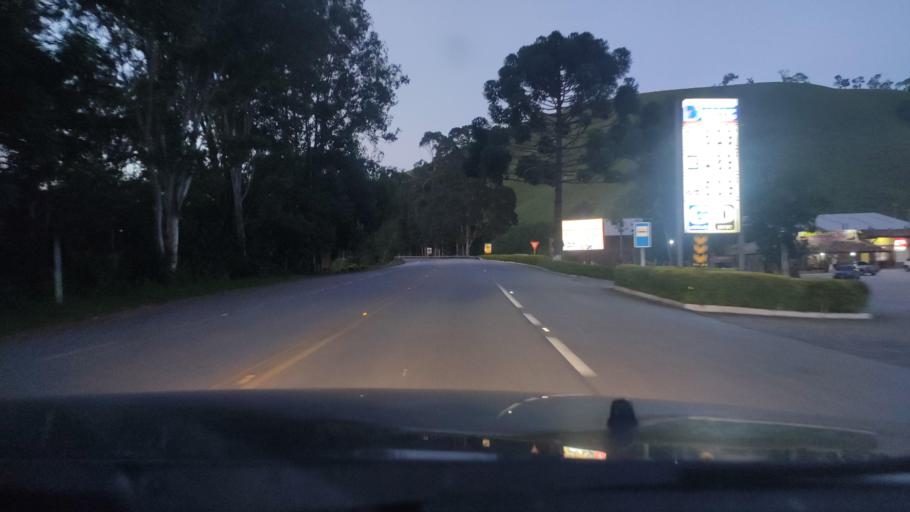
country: BR
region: Sao Paulo
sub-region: Campos Do Jordao
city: Campos do Jordao
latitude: -22.7227
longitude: -45.7268
